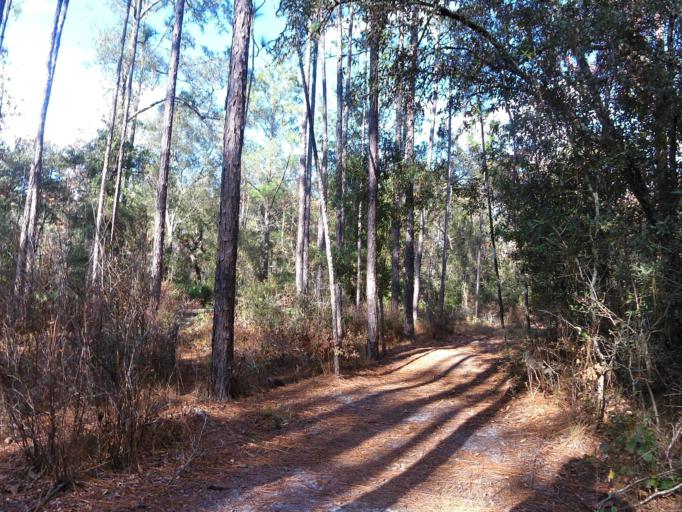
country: US
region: Florida
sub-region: Clay County
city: Middleburg
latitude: 30.1430
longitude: -81.9577
